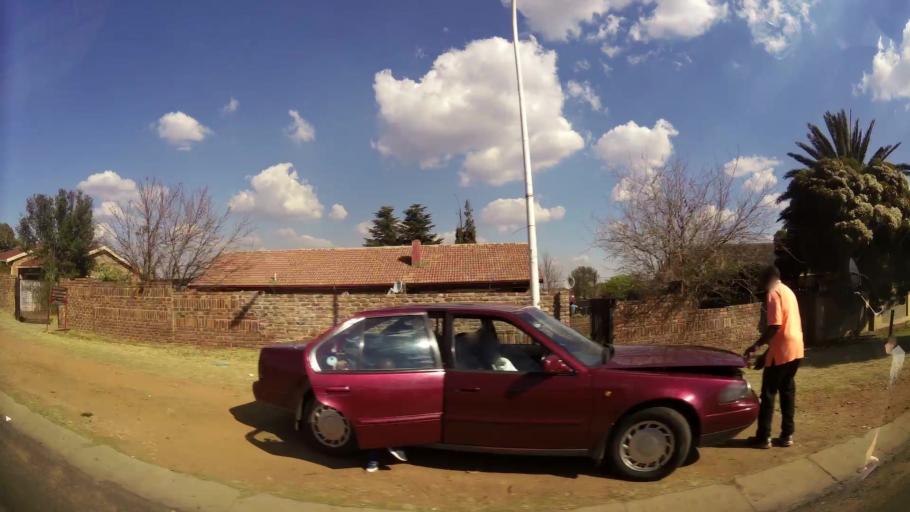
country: ZA
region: Mpumalanga
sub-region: Nkangala District Municipality
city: Witbank
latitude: -25.9270
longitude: 29.2399
